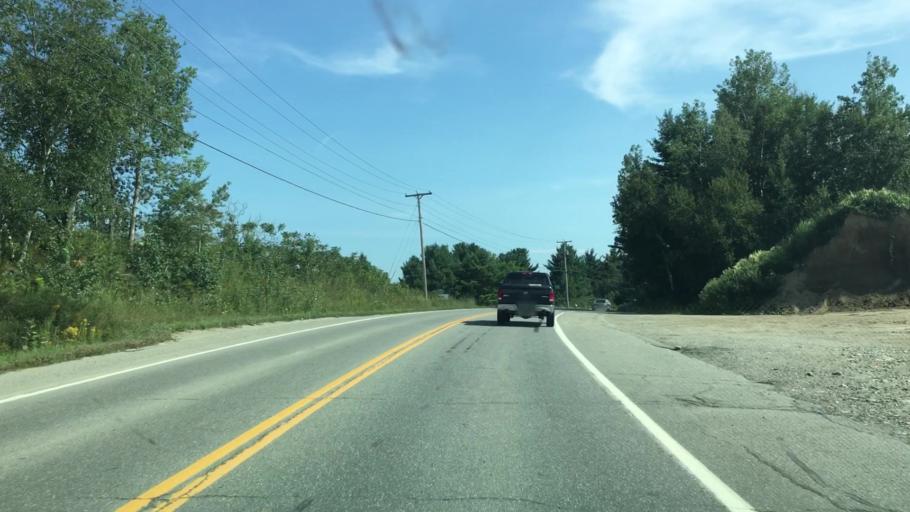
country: US
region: Maine
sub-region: Waldo County
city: Frankfort
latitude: 44.5566
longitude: -68.8650
